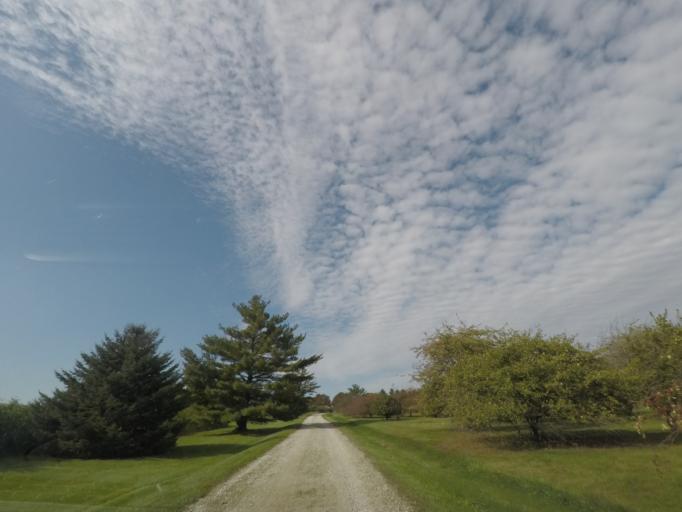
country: US
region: Iowa
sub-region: Story County
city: Gilbert
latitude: 42.1094
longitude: -93.5847
